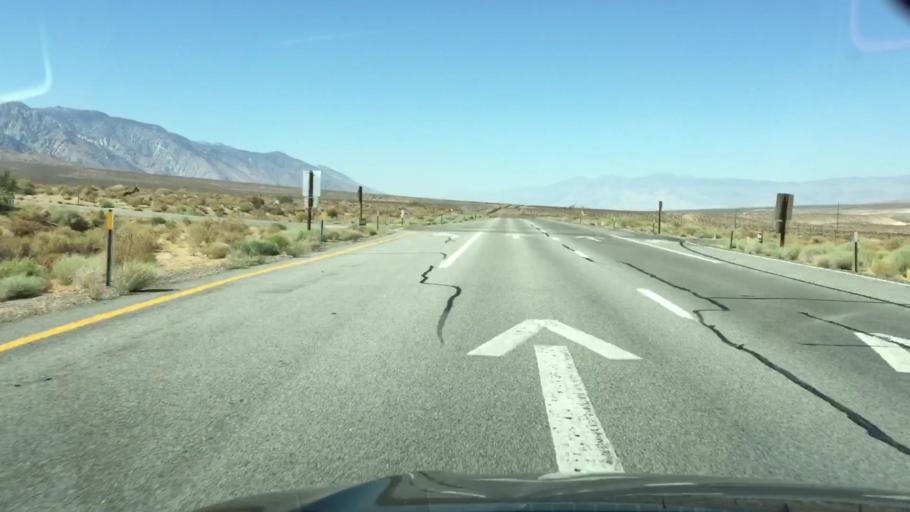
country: US
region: California
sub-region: Inyo County
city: Lone Pine
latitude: 36.1530
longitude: -117.9753
